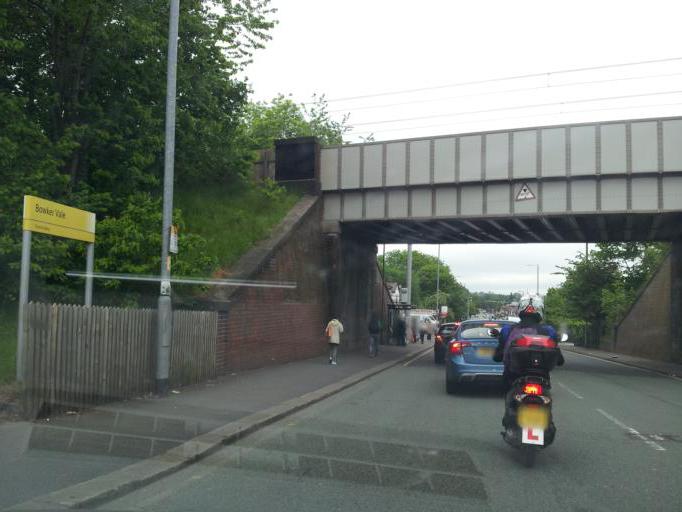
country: GB
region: England
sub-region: Manchester
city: Crumpsall
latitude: 53.5243
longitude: -2.2489
